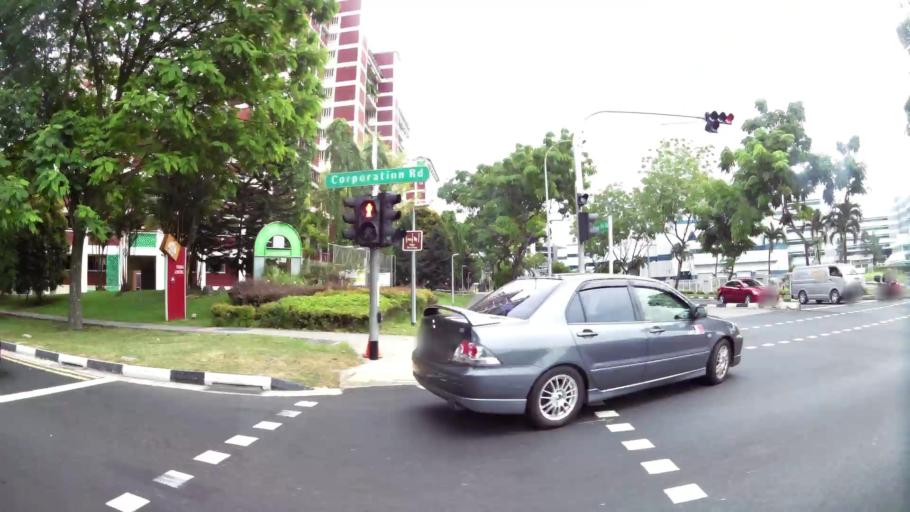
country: SG
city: Singapore
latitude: 1.3273
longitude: 103.7199
